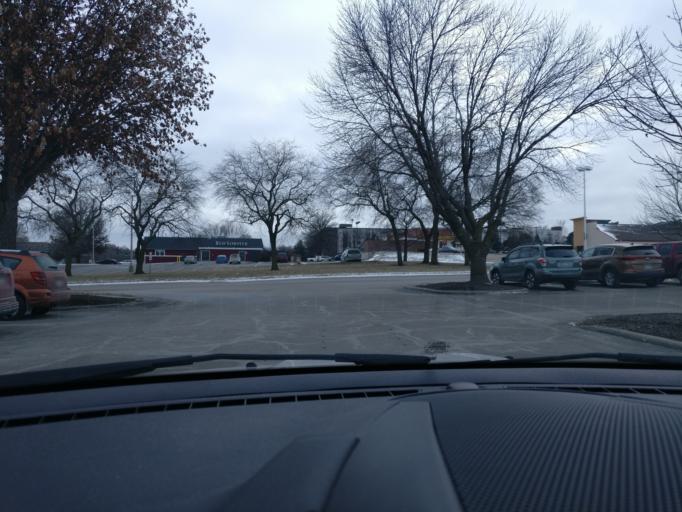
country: US
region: Nebraska
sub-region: Lancaster County
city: Lincoln
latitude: 40.8152
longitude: -96.6314
